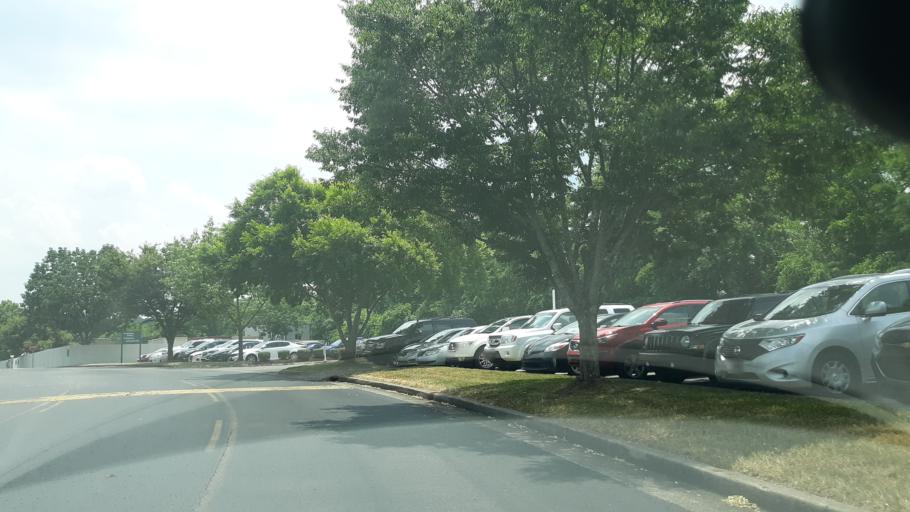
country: US
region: Tennessee
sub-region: Davidson County
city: Lakewood
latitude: 36.1774
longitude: -86.6098
